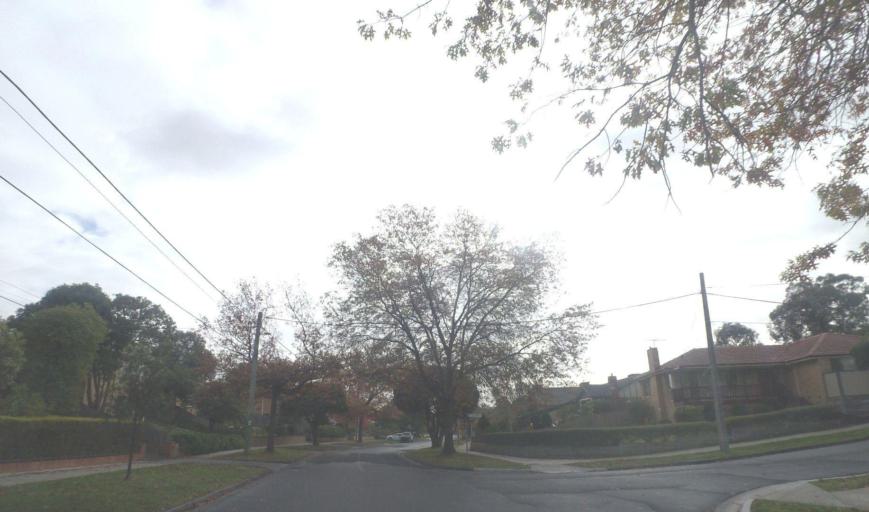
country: AU
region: Victoria
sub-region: Whitehorse
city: Nunawading
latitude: -37.8099
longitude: 145.1752
